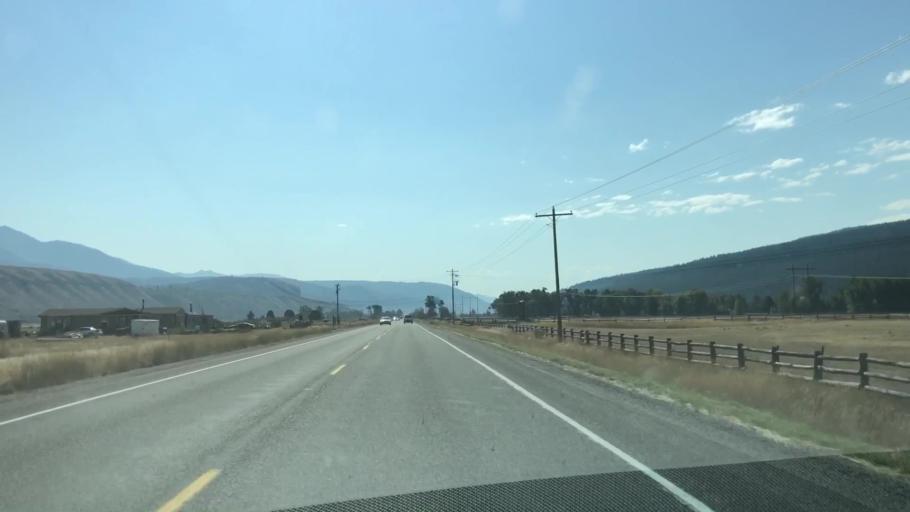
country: US
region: Idaho
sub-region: Teton County
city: Victor
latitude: 43.3976
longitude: -111.2818
